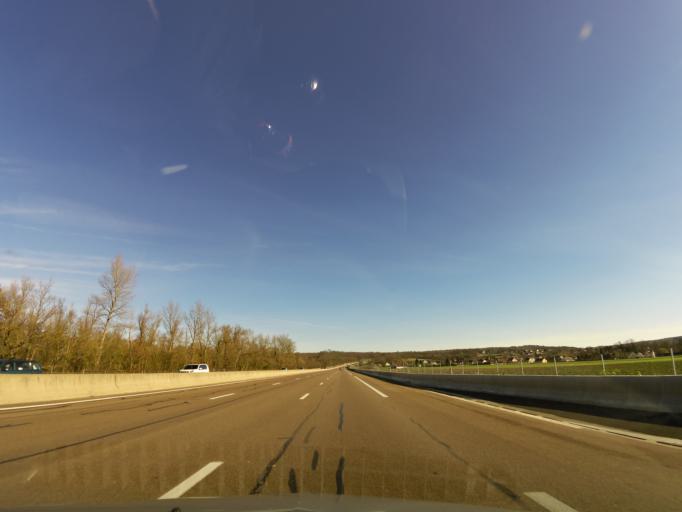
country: FR
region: Bourgogne
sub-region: Departement de l'Yonne
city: Gurgy
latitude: 47.8563
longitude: 3.5689
